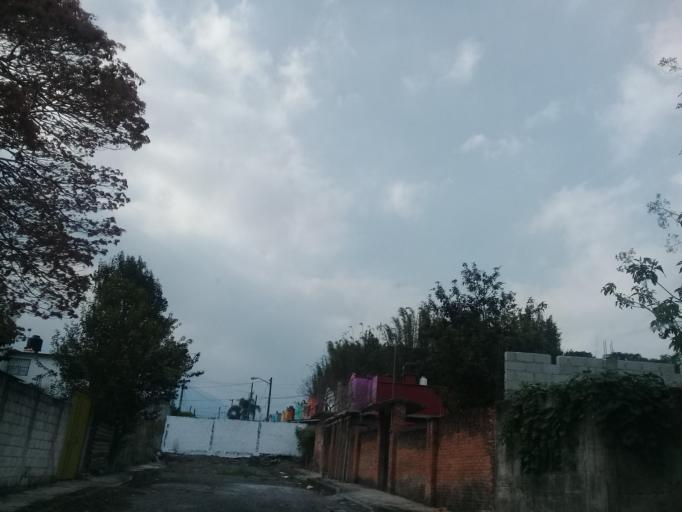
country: MX
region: Veracruz
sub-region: Mariano Escobedo
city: Palmira
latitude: 18.8727
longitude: -97.1068
